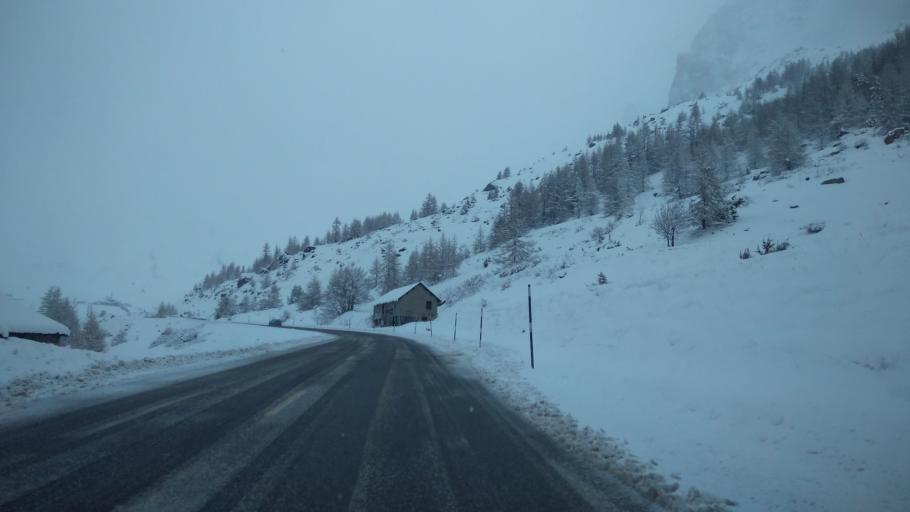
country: FR
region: Provence-Alpes-Cote d'Azur
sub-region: Departement des Hautes-Alpes
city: Le Monetier-les-Bains
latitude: 45.0279
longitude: 6.4478
